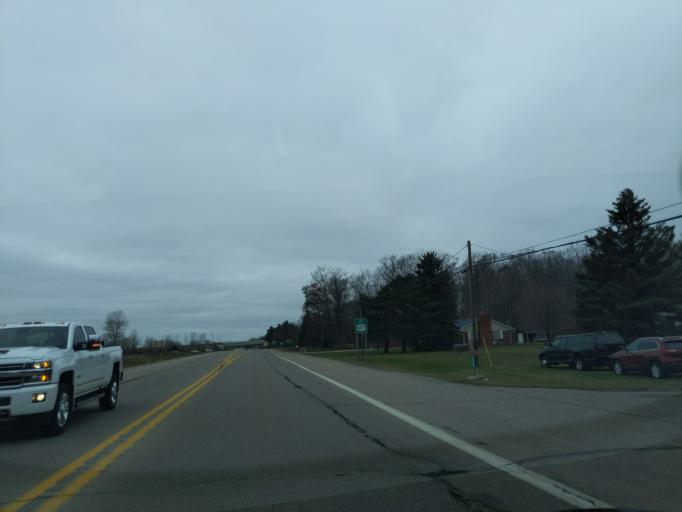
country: US
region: Michigan
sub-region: Clinton County
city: Saint Johns
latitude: 43.0013
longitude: -84.5119
